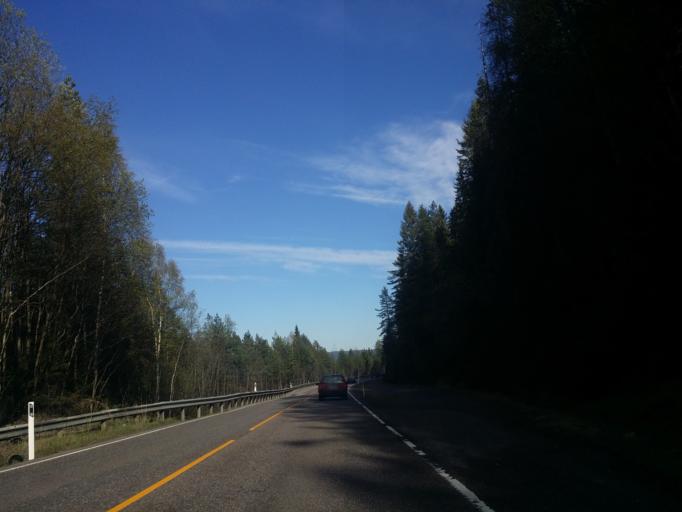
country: NO
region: Buskerud
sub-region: Kongsberg
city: Kongsberg
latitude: 59.6291
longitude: 9.5673
